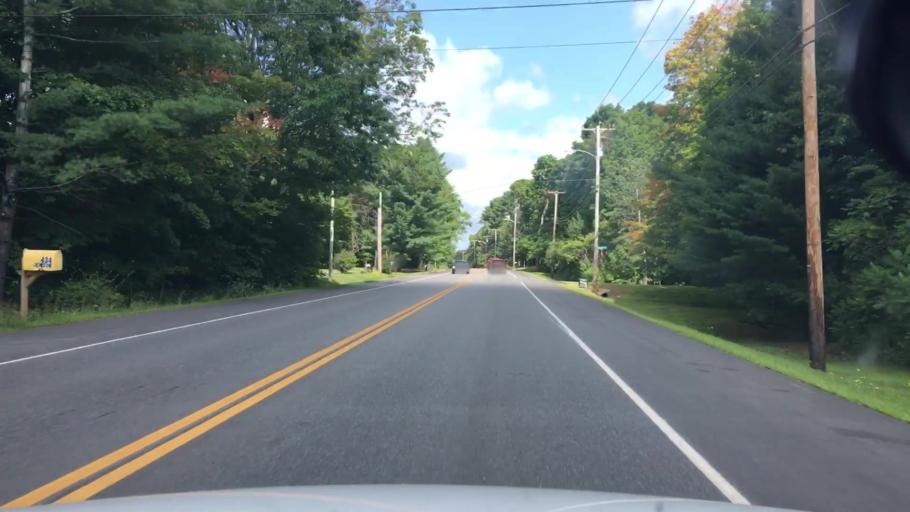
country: US
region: Maine
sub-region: Kennebec County
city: Waterville
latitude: 44.5778
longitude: -69.6450
